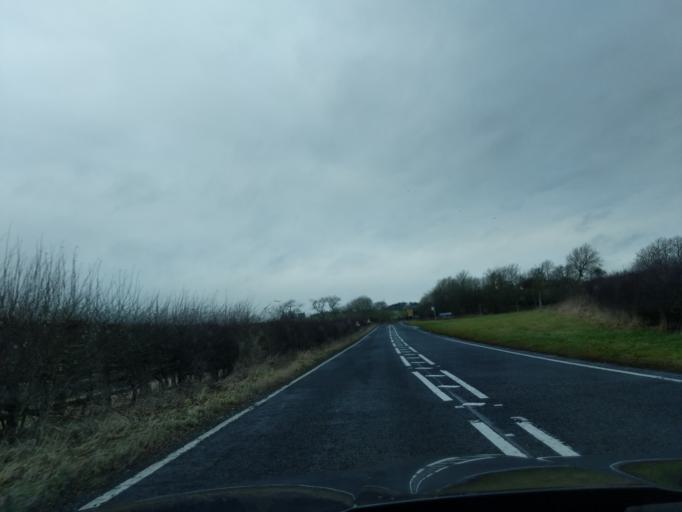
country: GB
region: England
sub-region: Northumberland
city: Rothley
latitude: 55.1550
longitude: -2.0118
